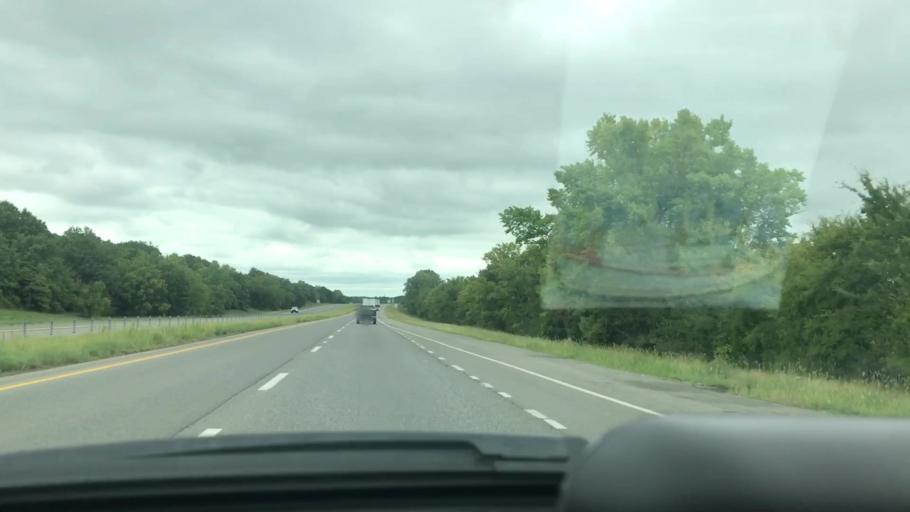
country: US
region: Oklahoma
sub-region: McIntosh County
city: Eufaula
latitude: 35.3667
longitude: -95.5727
